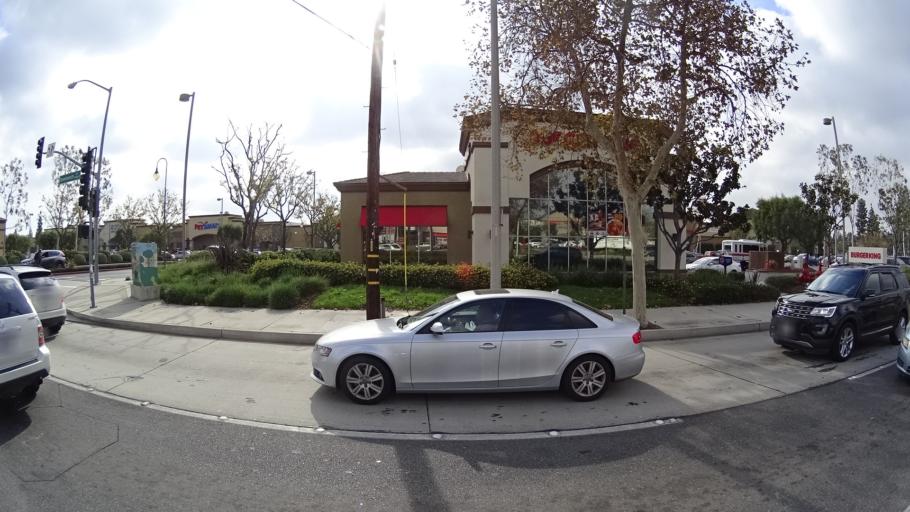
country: US
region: California
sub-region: Orange County
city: Tustin
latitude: 33.7598
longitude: -117.8373
